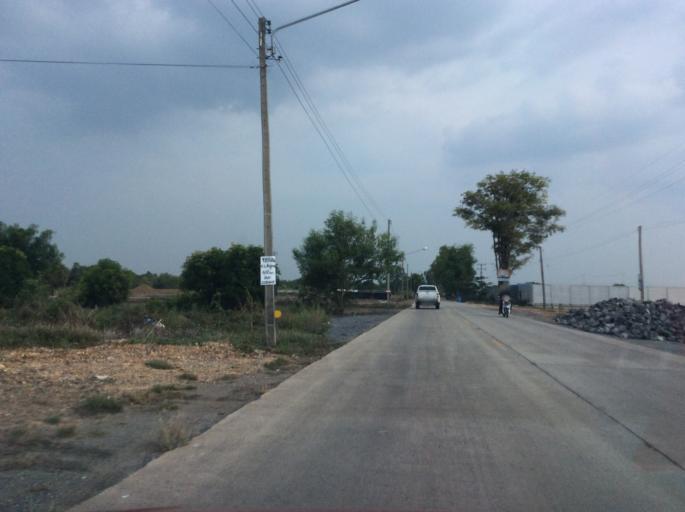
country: TH
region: Pathum Thani
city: Thanyaburi
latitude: 13.9778
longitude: 100.7266
